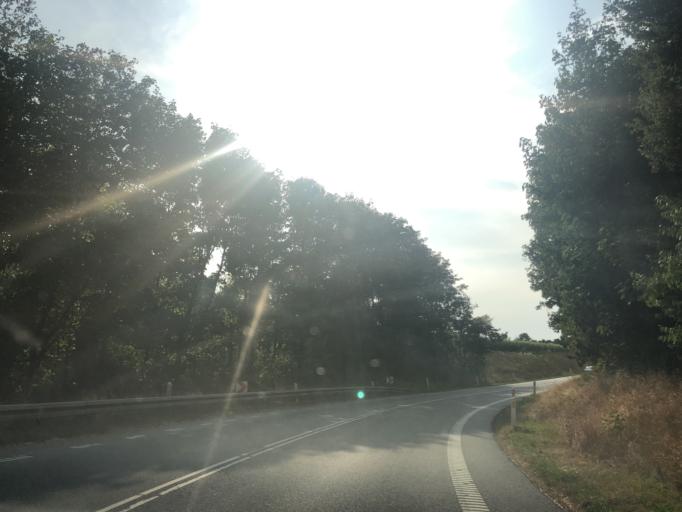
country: DK
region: Central Jutland
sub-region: Skive Kommune
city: Skive
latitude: 56.6271
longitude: 8.9000
